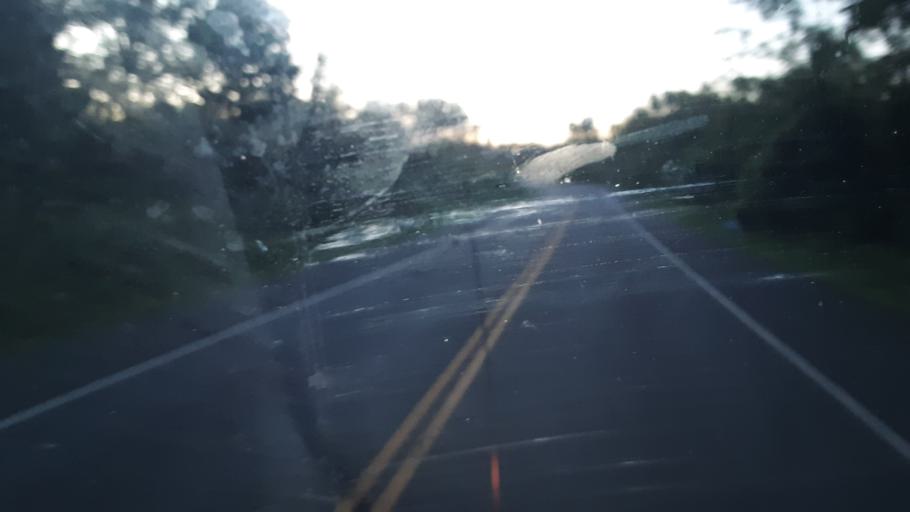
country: US
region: New York
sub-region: Montgomery County
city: Hagaman
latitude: 42.9508
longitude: -74.1240
